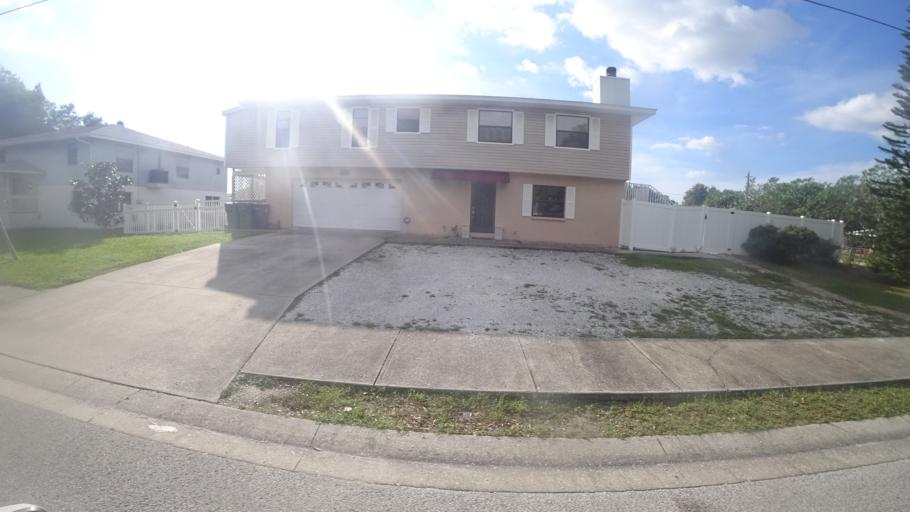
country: US
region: Florida
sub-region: Manatee County
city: Palmetto
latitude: 27.5211
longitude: -82.5892
